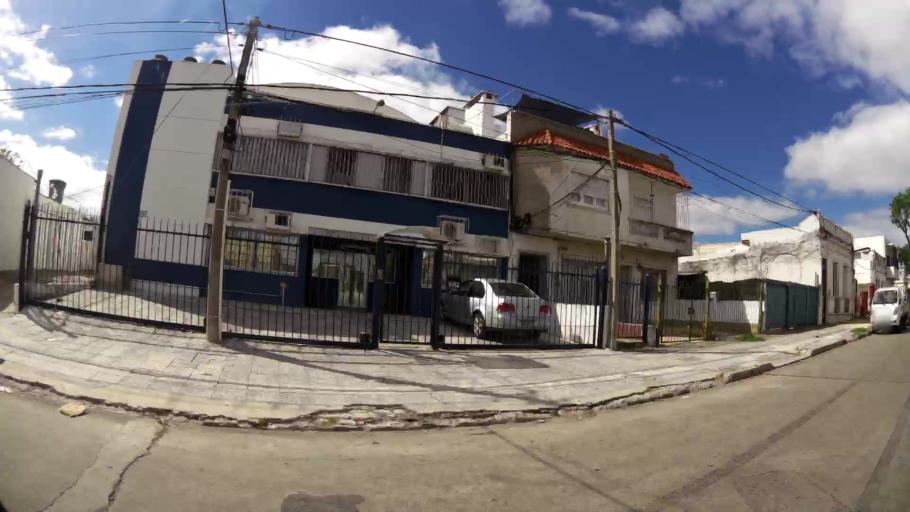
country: UY
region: Montevideo
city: Montevideo
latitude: -34.8804
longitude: -56.1355
